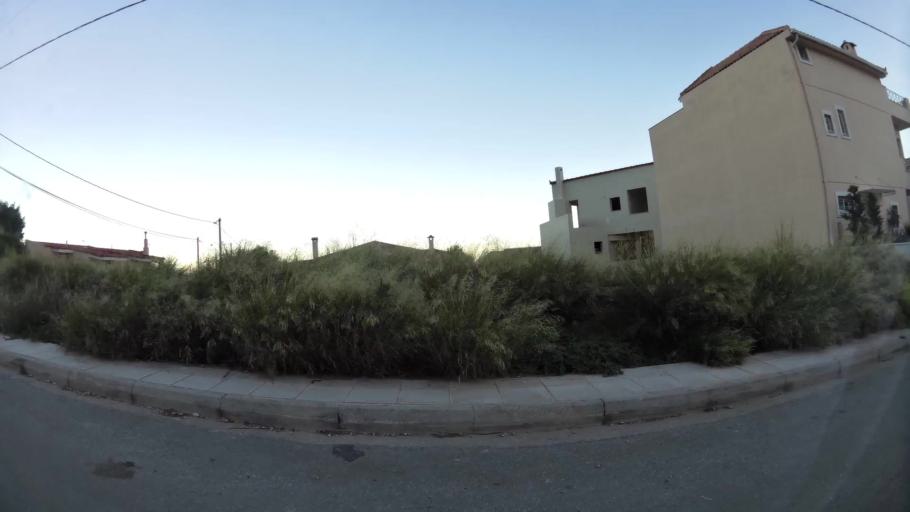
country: GR
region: Attica
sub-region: Nomarchia Anatolikis Attikis
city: Paiania
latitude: 37.9557
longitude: 23.8444
